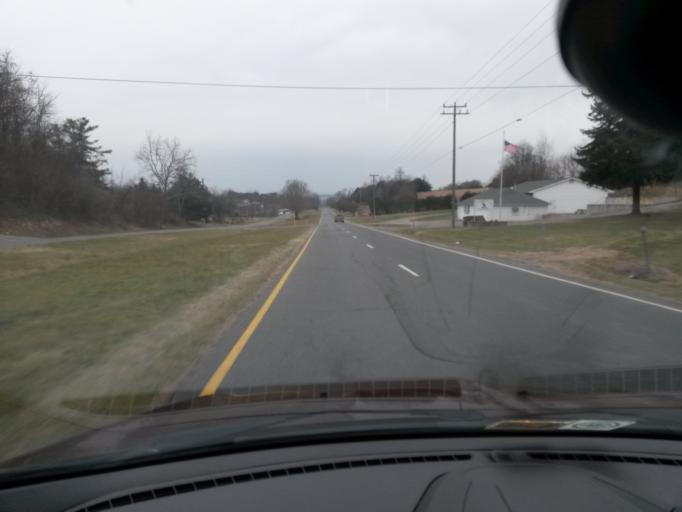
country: US
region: Virginia
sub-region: City of Buena Vista
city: Buena Vista
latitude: 37.8913
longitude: -79.2627
